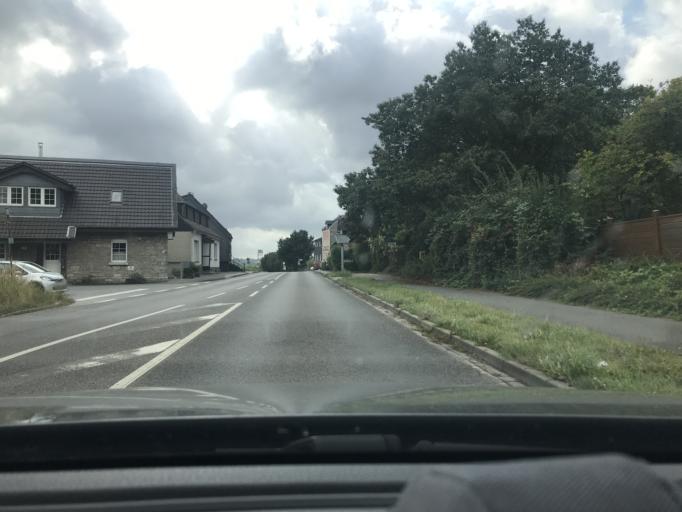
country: DE
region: North Rhine-Westphalia
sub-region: Regierungsbezirk Dusseldorf
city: Mettmann
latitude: 51.2323
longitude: 6.9986
